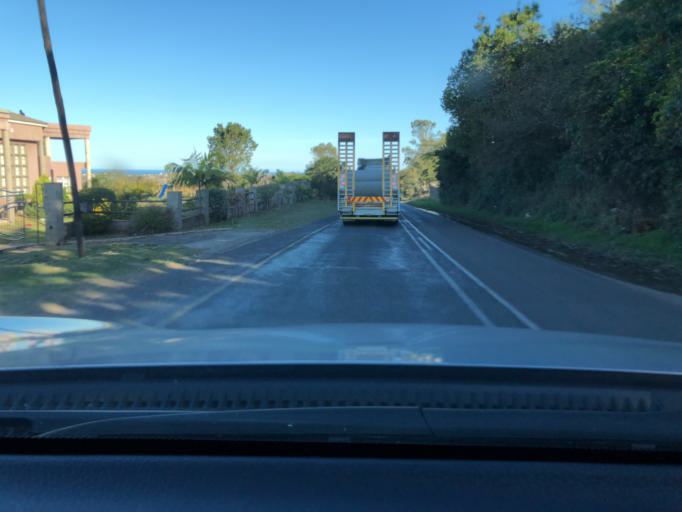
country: ZA
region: KwaZulu-Natal
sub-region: eThekwini Metropolitan Municipality
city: Umkomaas
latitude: -30.0236
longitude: 30.8117
